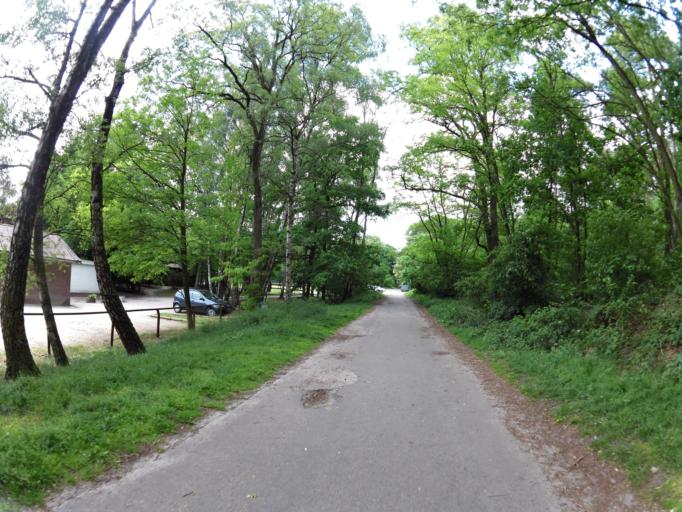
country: NL
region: Limburg
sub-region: Gemeente Brunssum
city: Brunssum
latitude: 50.9350
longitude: 5.9963
